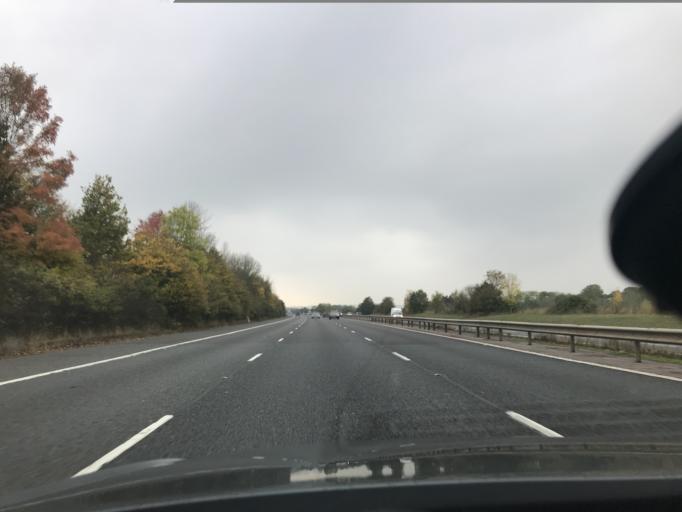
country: GB
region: England
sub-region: Oxfordshire
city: Wheatley
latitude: 51.7817
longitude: -1.0939
